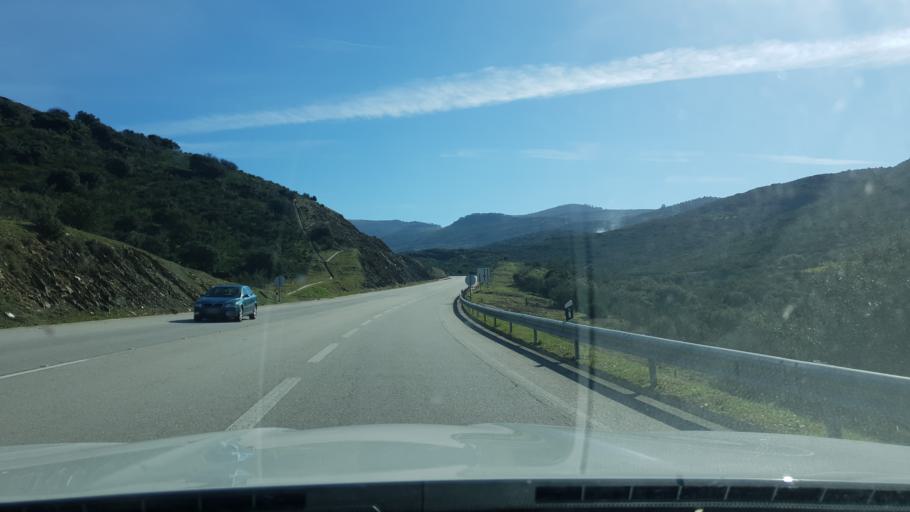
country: PT
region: Braganca
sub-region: Torre de Moncorvo
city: Torre de Moncorvo
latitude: 41.1842
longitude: -7.0922
